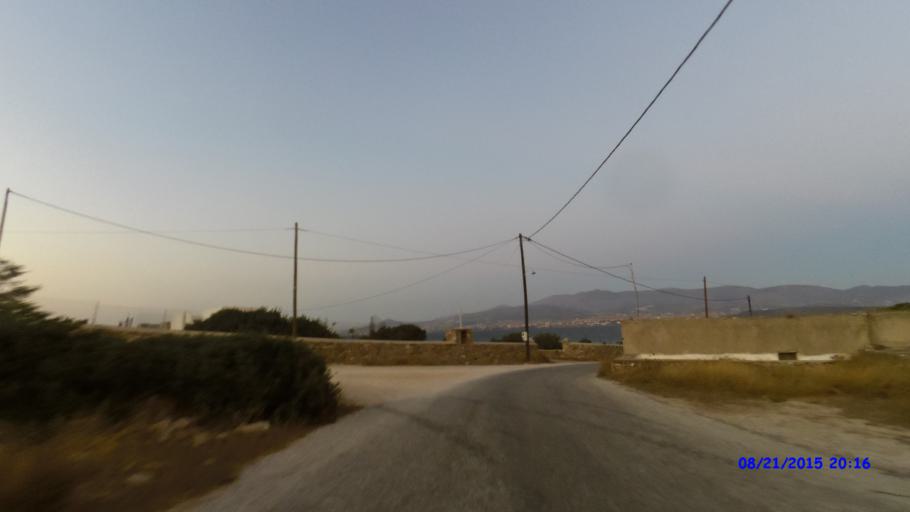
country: GR
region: South Aegean
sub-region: Nomos Kykladon
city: Antiparos
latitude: 37.0095
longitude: 25.0739
